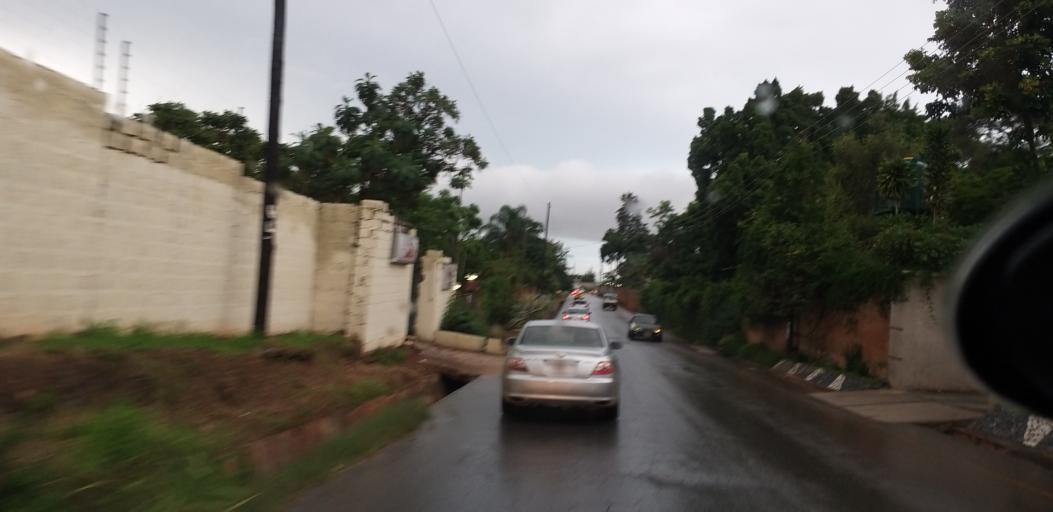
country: ZM
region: Lusaka
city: Lusaka
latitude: -15.4175
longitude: 28.3660
